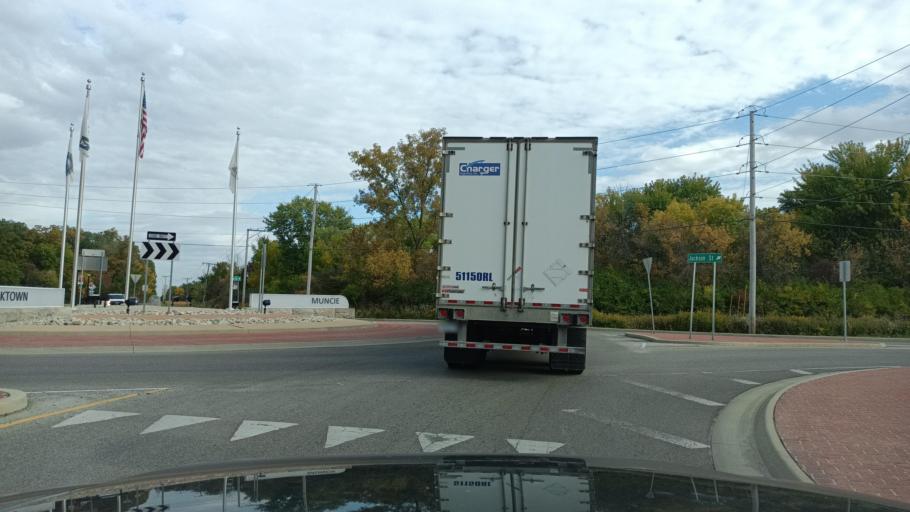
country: US
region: Indiana
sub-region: Delaware County
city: Yorktown
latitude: 40.2052
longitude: -85.4625
